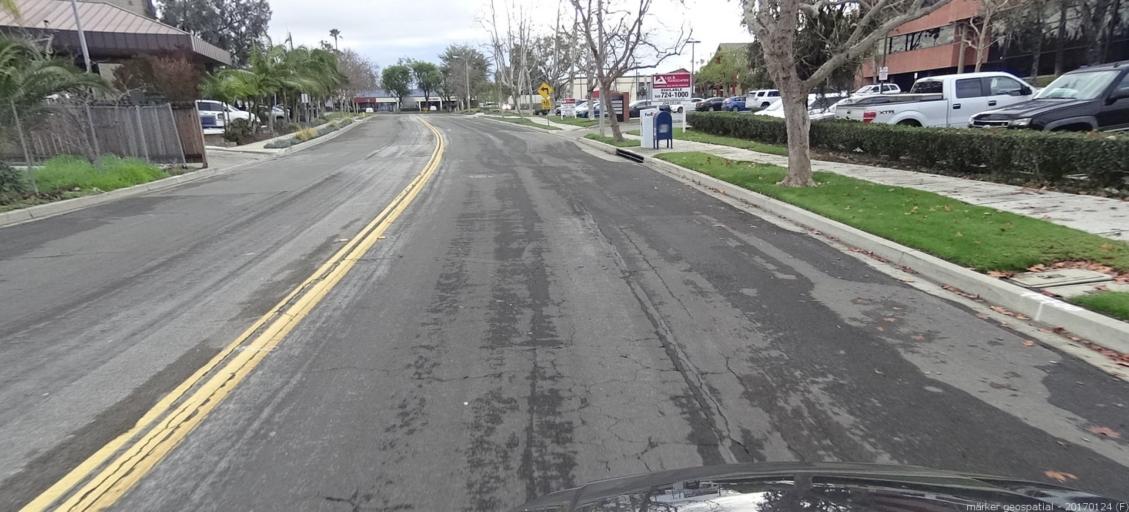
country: US
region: California
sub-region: Orange County
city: Laguna Hills
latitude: 33.6261
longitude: -117.7165
